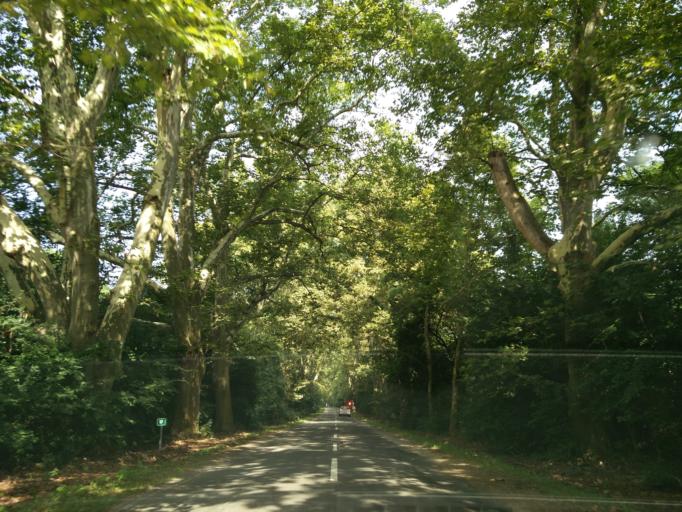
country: HU
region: Fejer
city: Bicske
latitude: 47.4359
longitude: 18.6153
